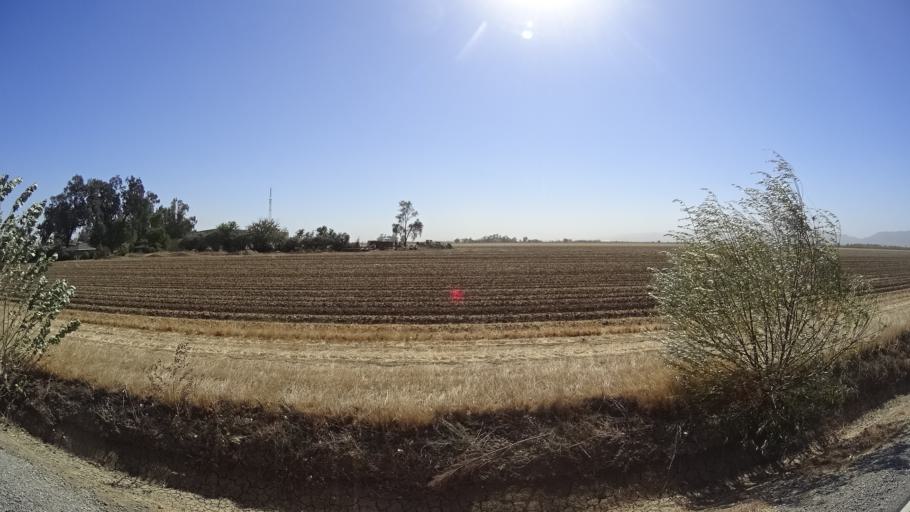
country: US
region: California
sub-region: Yolo County
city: Winters
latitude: 38.5840
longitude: -121.9358
